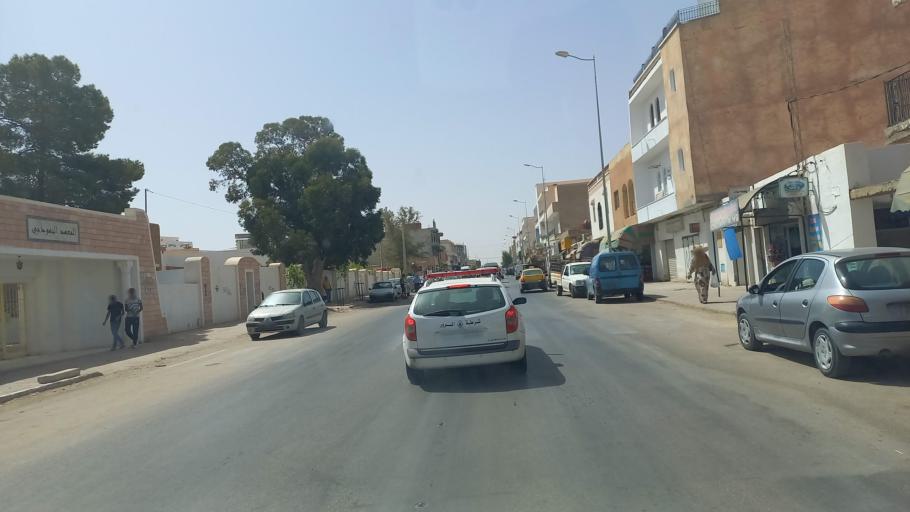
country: TN
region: Madanin
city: Medenine
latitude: 33.3353
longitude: 10.4856
